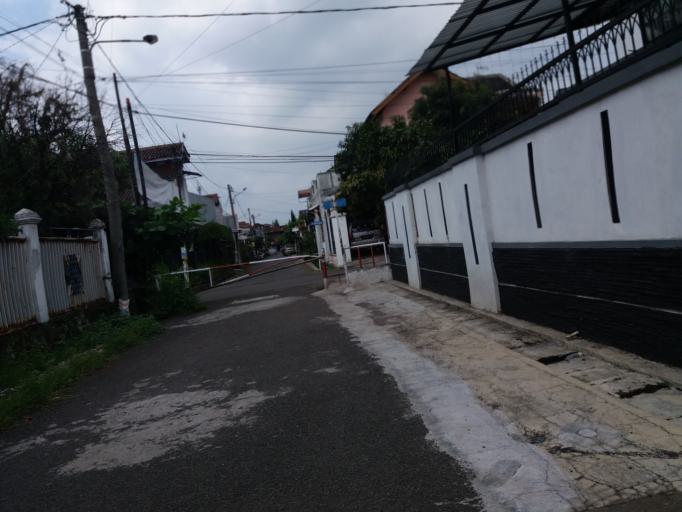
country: ID
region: West Java
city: Bandung
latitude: -6.9217
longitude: 107.6582
